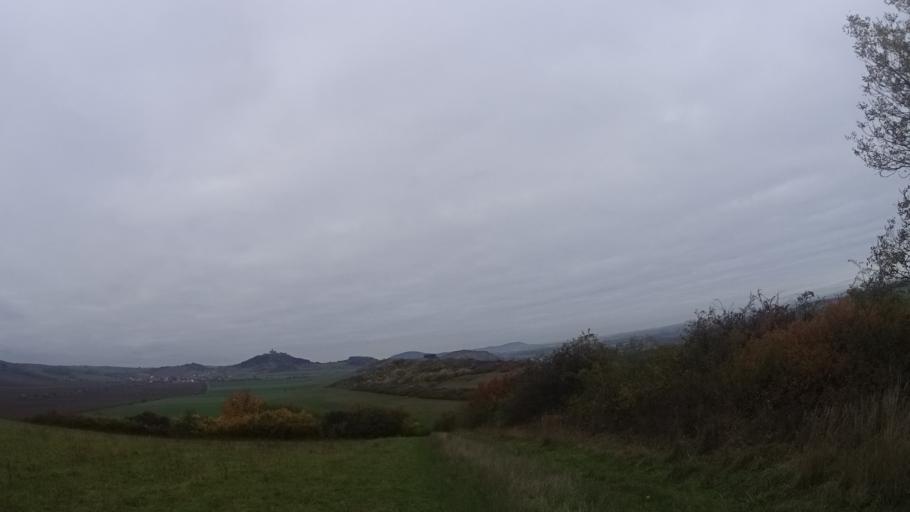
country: DE
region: Thuringia
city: Arnstadt
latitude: 50.8502
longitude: 10.9212
